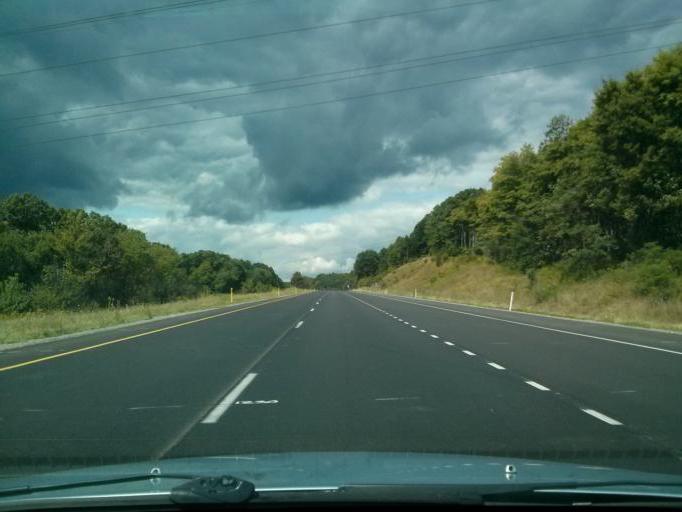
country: US
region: Pennsylvania
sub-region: Clarion County
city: Clarion
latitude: 41.1946
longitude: -79.4325
